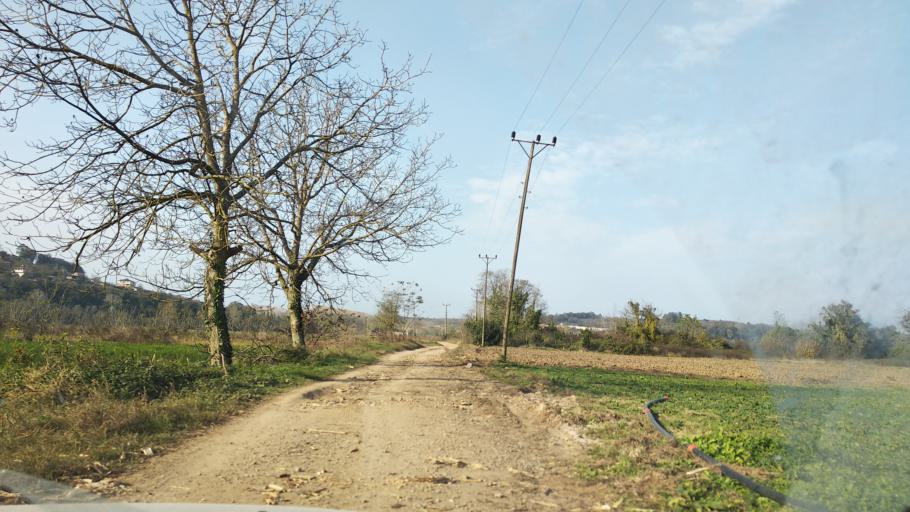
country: TR
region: Sakarya
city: Karasu
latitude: 41.0878
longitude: 30.5977
